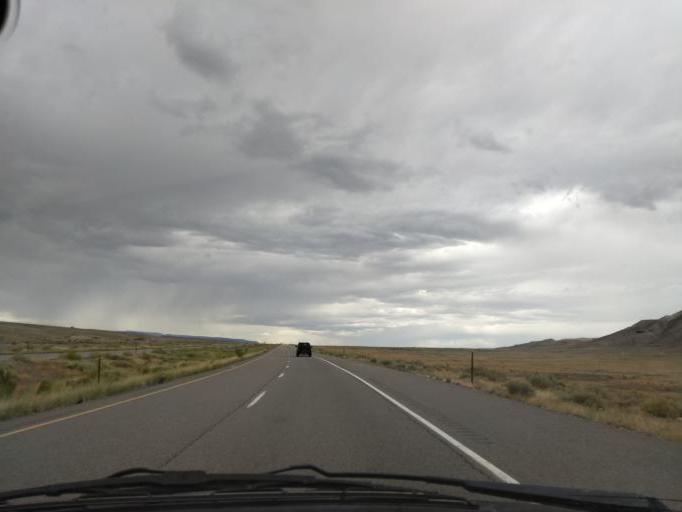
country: US
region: Colorado
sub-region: Delta County
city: Delta
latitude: 38.7775
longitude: -108.2322
